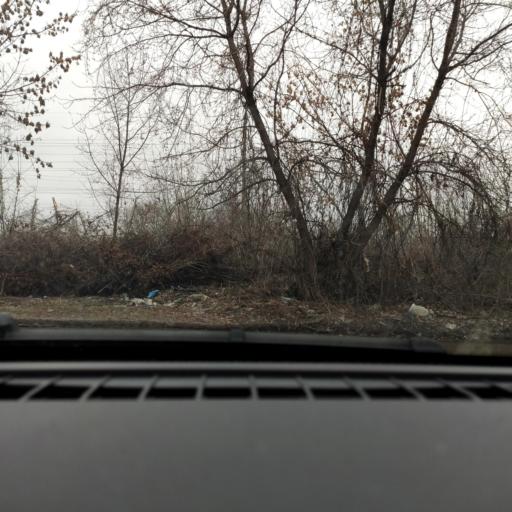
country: RU
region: Voronezj
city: Maslovka
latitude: 51.6114
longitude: 39.2732
